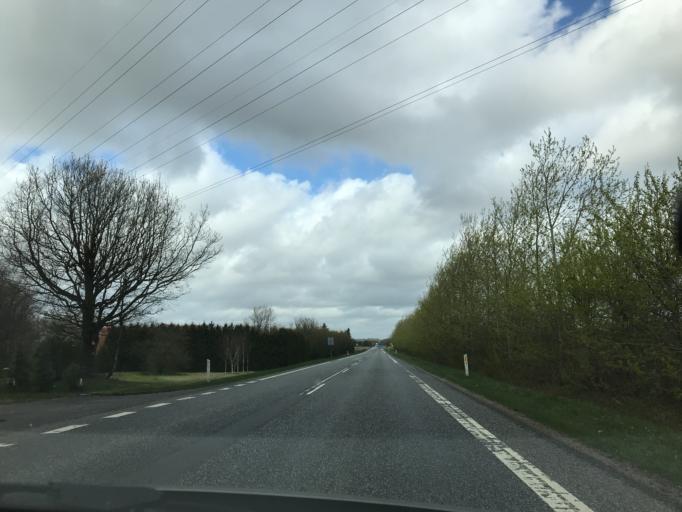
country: DK
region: Central Jutland
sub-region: Viborg Kommune
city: Stoholm
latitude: 56.3930
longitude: 8.9972
